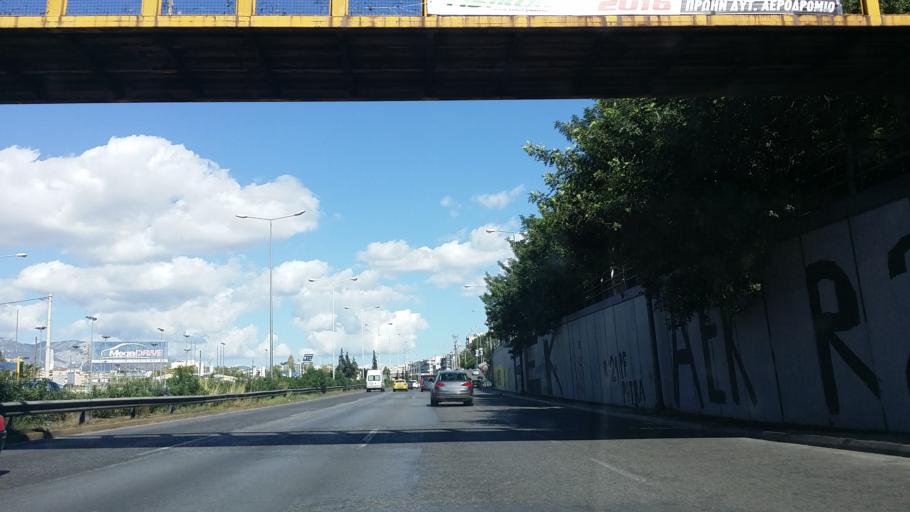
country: GR
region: Attica
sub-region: Nomarchia Athinas
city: Nea Chalkidona
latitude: 38.0330
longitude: 23.7304
